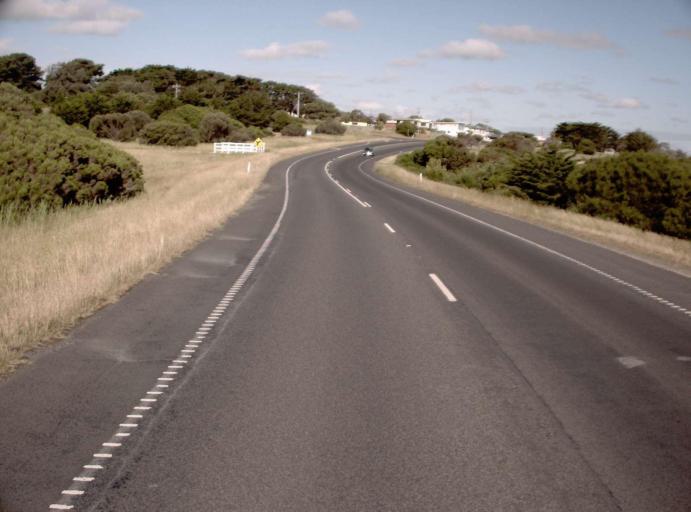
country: AU
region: Victoria
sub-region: Bass Coast
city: North Wonthaggi
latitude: -38.5472
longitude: 145.4700
